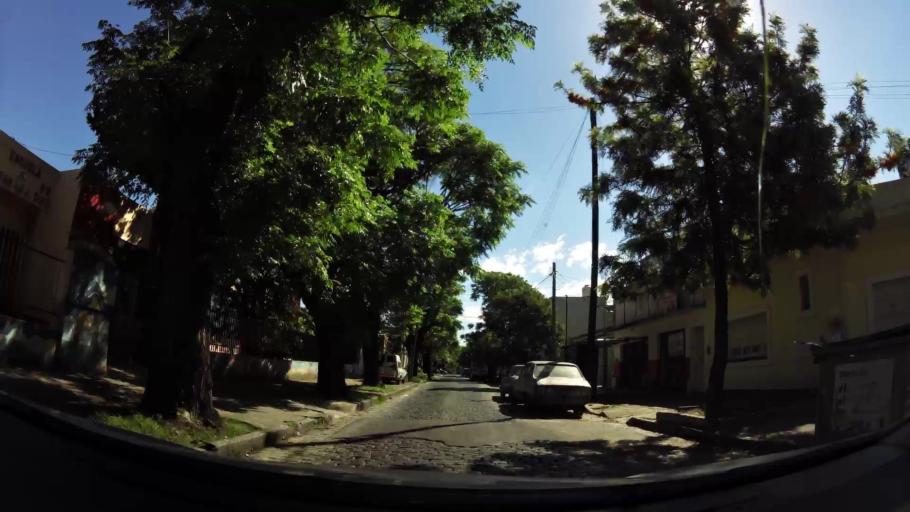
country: AR
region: Buenos Aires
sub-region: Partido de San Isidro
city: San Isidro
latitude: -34.4645
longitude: -58.5323
